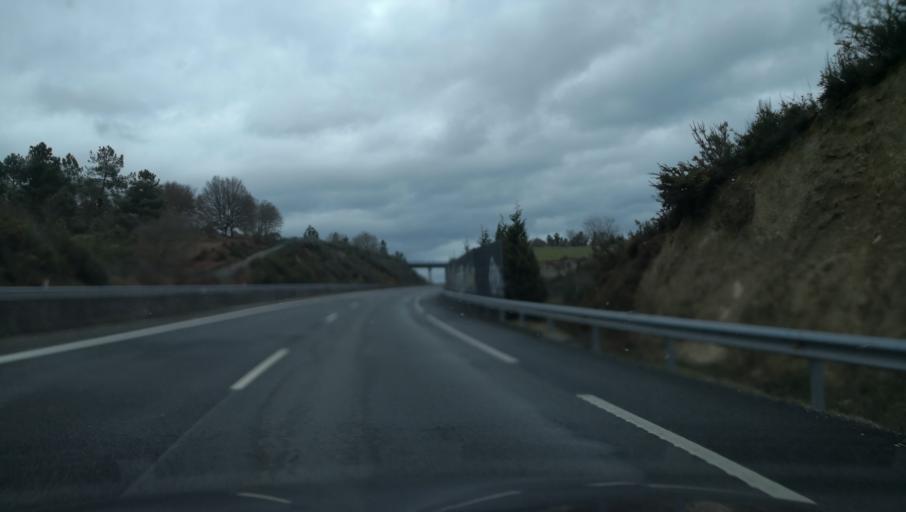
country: ES
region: Galicia
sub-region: Provincia de Ourense
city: Pinor
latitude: 42.5018
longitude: -8.0275
